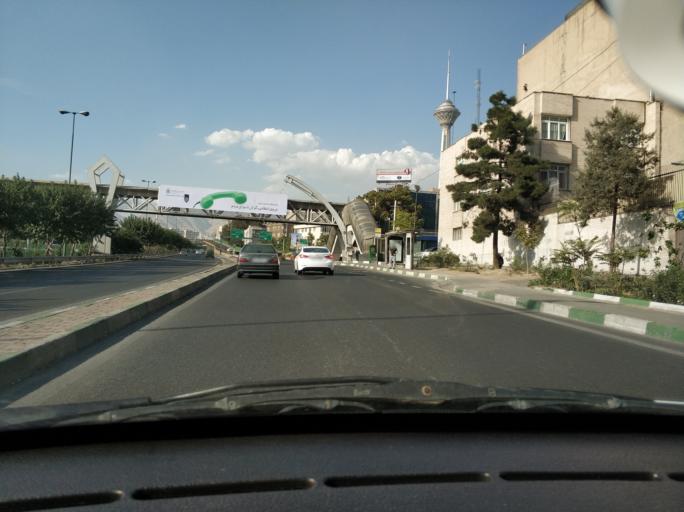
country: IR
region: Tehran
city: Tehran
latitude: 35.7335
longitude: 51.3715
